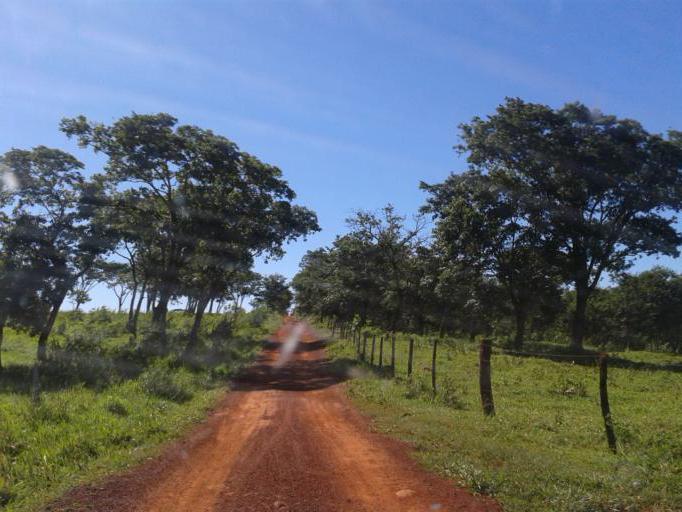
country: BR
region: Minas Gerais
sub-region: Capinopolis
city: Capinopolis
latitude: -18.6763
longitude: -49.5832
